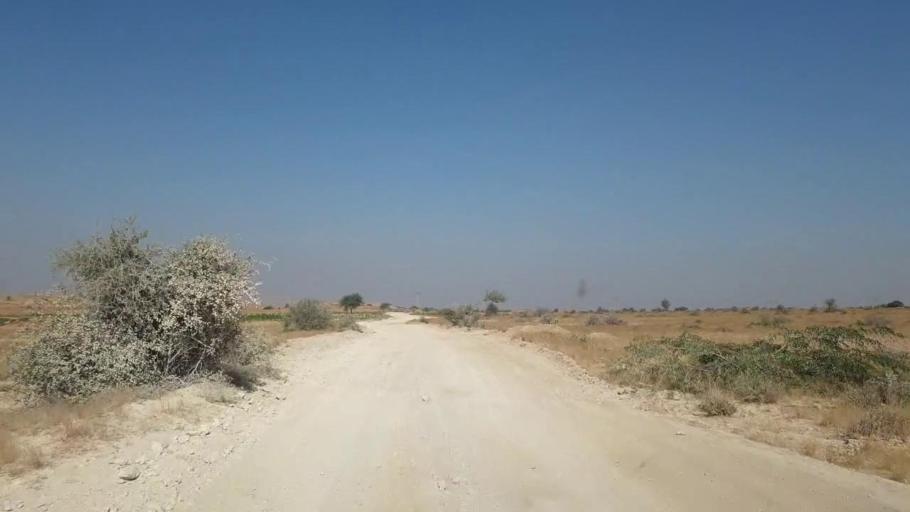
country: PK
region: Sindh
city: Thatta
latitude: 25.2342
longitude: 67.8042
